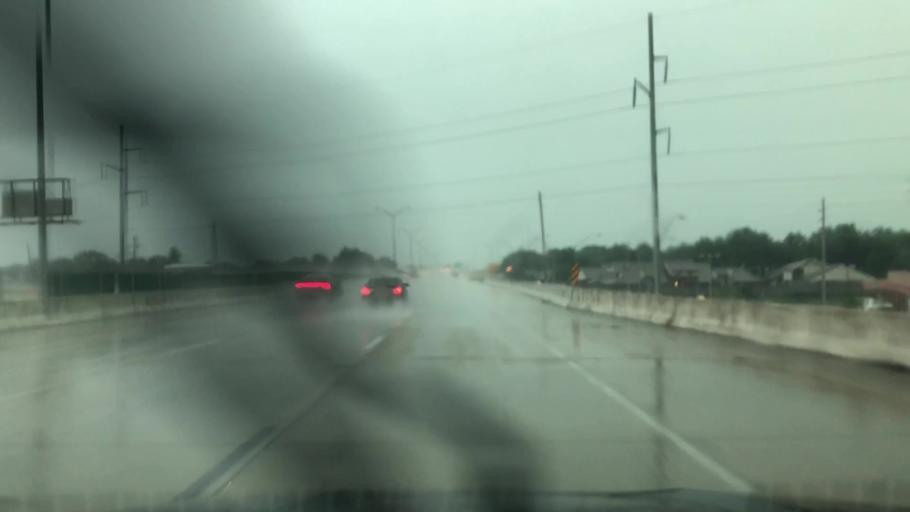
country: US
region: Oklahoma
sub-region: Tulsa County
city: Broken Arrow
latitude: 36.1463
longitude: -95.8503
